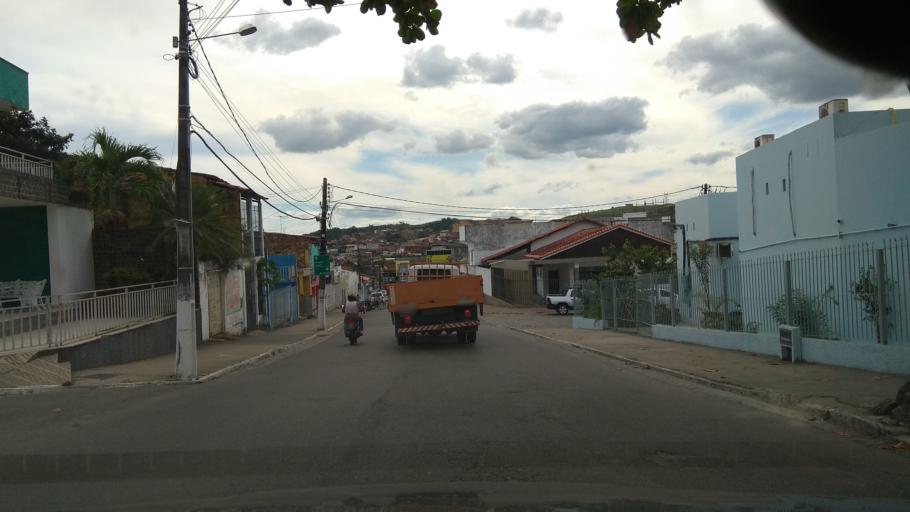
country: BR
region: Bahia
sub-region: Ipiau
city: Ipiau
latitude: -14.1363
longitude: -39.7368
